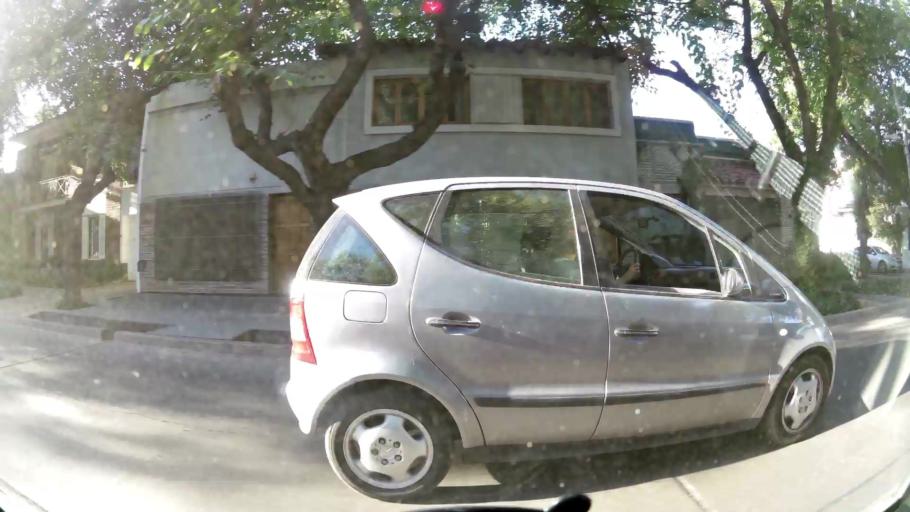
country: AR
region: Mendoza
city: Mendoza
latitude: -32.9037
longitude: -68.8454
